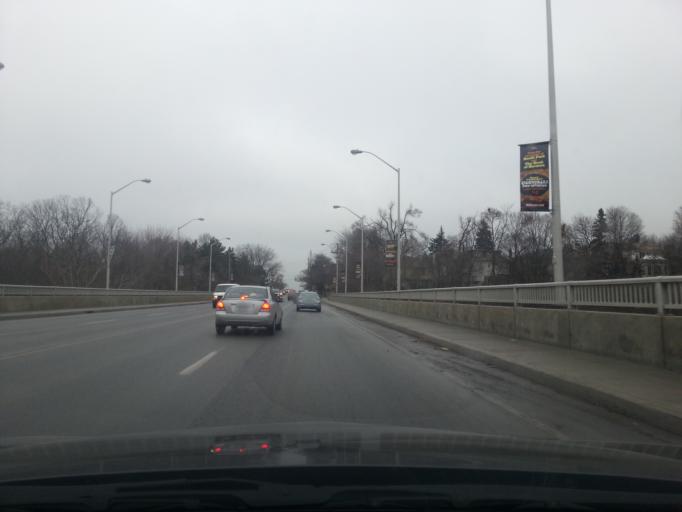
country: CA
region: Ontario
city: Toronto
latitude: 43.6900
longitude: -79.4210
